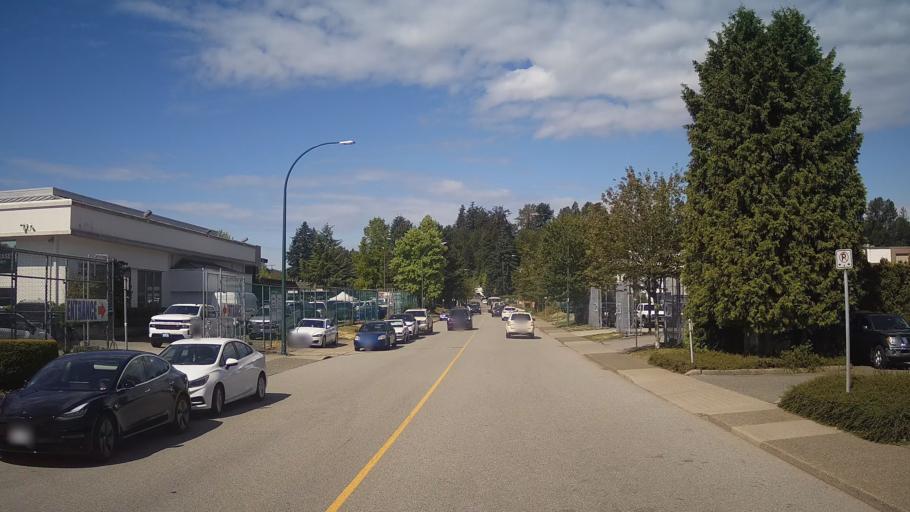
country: CA
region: British Columbia
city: Port Moody
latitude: 49.2789
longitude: -122.8161
